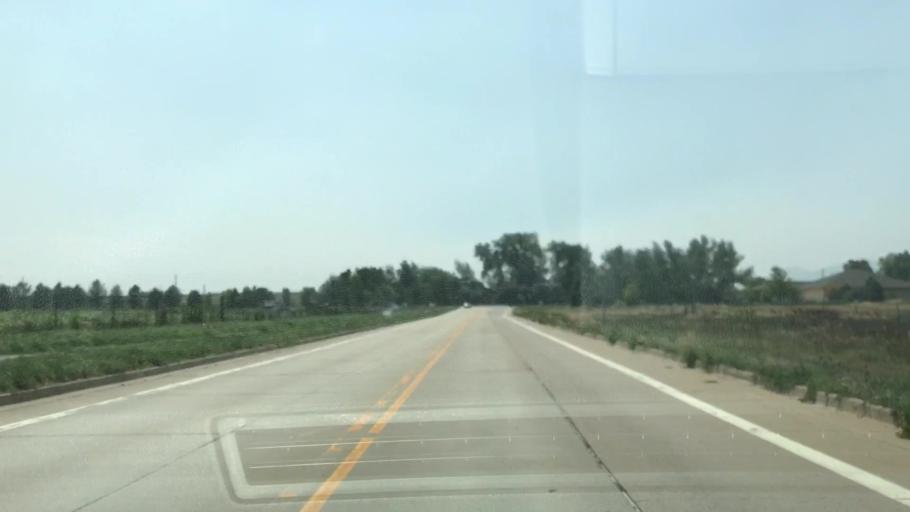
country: US
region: Colorado
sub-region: Boulder County
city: Gunbarrel
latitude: 40.0536
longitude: -105.2161
